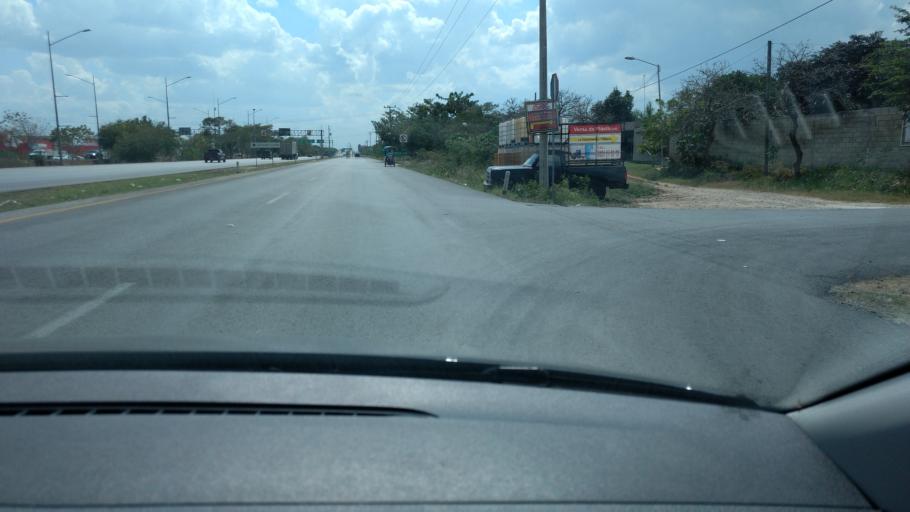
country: MX
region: Yucatan
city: Merida
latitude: 20.9929
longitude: -89.5625
